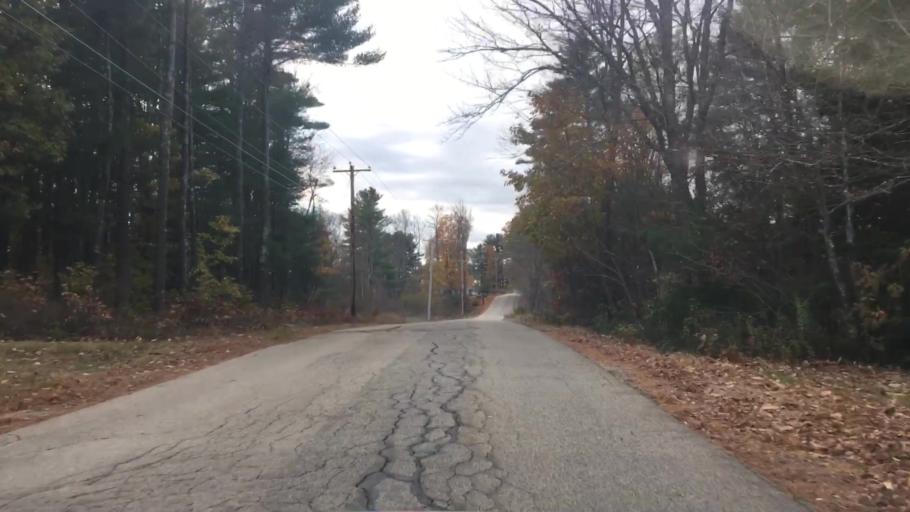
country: US
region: Maine
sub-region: York County
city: Springvale
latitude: 43.4620
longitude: -70.8358
